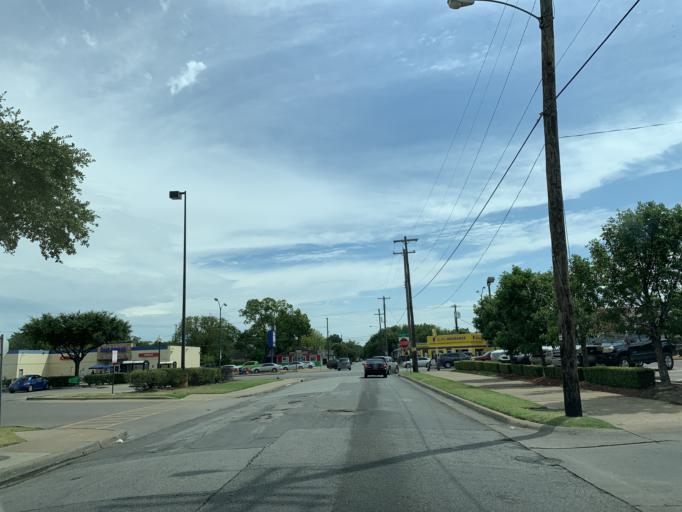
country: US
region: Texas
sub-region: Dallas County
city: Dallas
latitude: 32.7438
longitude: -96.8340
